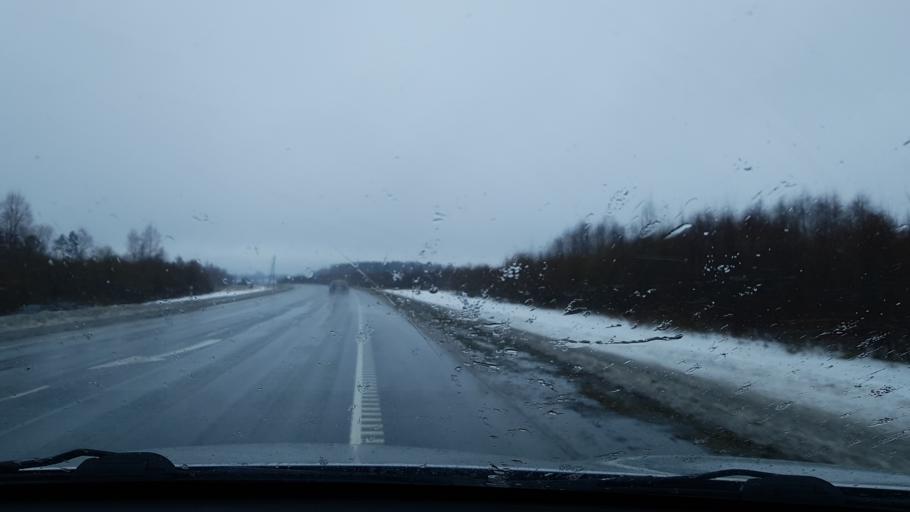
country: EE
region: Raplamaa
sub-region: Kohila vald
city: Kohila
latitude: 59.1766
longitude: 24.7764
